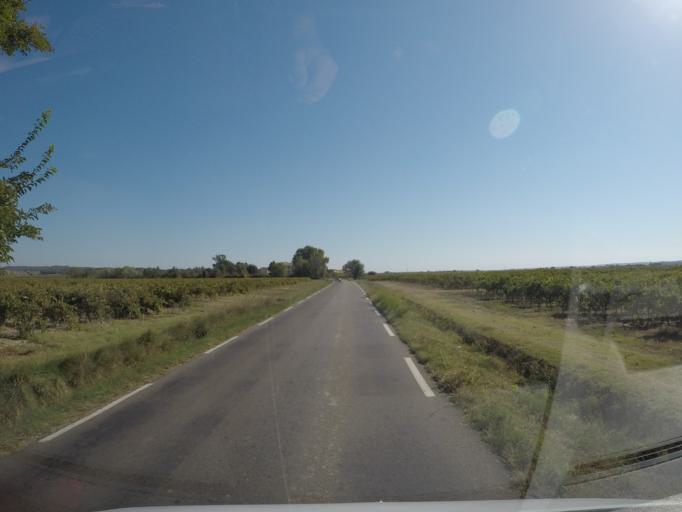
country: FR
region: Languedoc-Roussillon
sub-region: Departement du Gard
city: Saint-Chaptes
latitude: 43.9824
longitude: 4.2581
